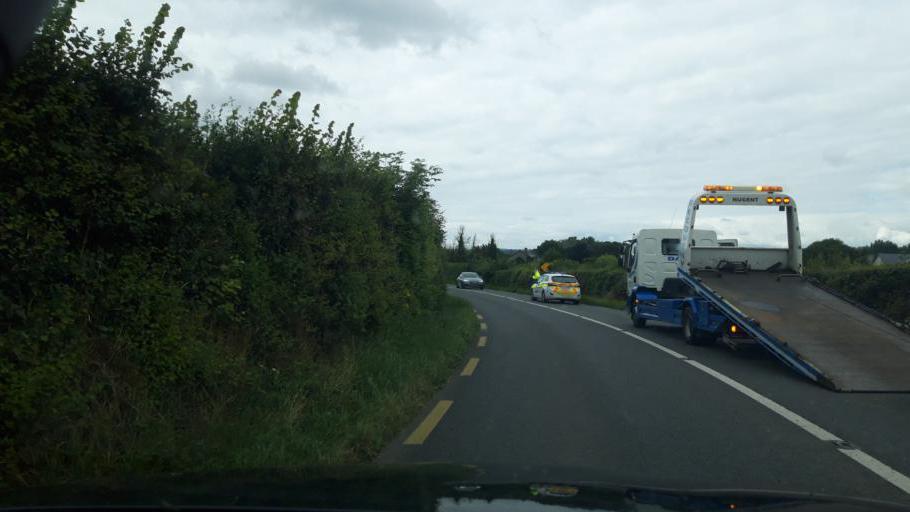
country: IE
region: Leinster
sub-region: Kilkenny
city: Thomastown
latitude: 52.6237
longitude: -7.0703
